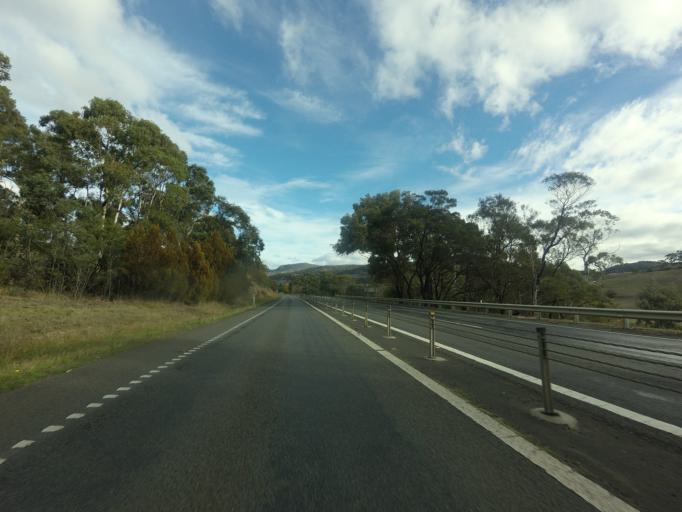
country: AU
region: Tasmania
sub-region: Brighton
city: Bridgewater
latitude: -42.5875
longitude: 147.2249
